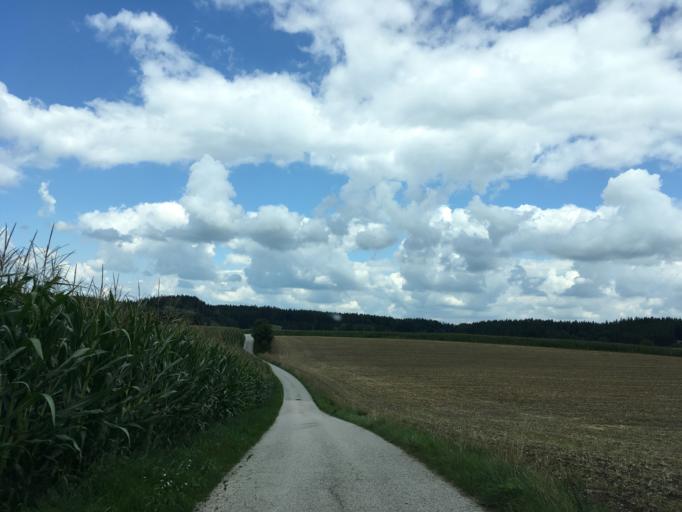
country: DE
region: Bavaria
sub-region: Upper Bavaria
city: Schnaitsee
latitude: 48.0477
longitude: 12.3366
